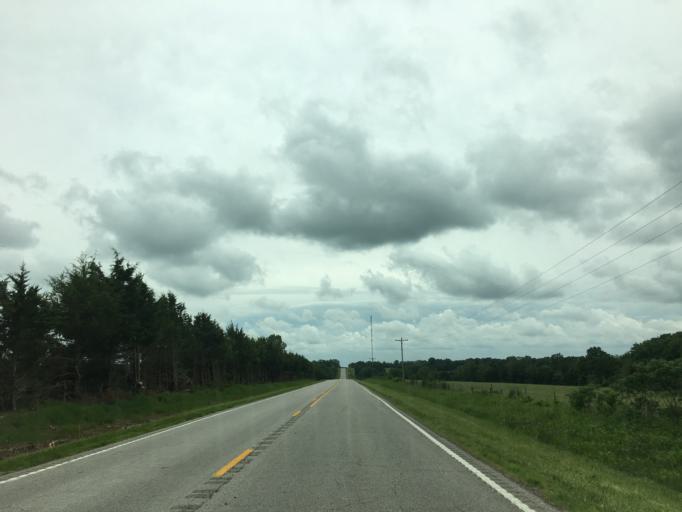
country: US
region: Missouri
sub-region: Gasconade County
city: Owensville
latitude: 38.4990
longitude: -91.4619
